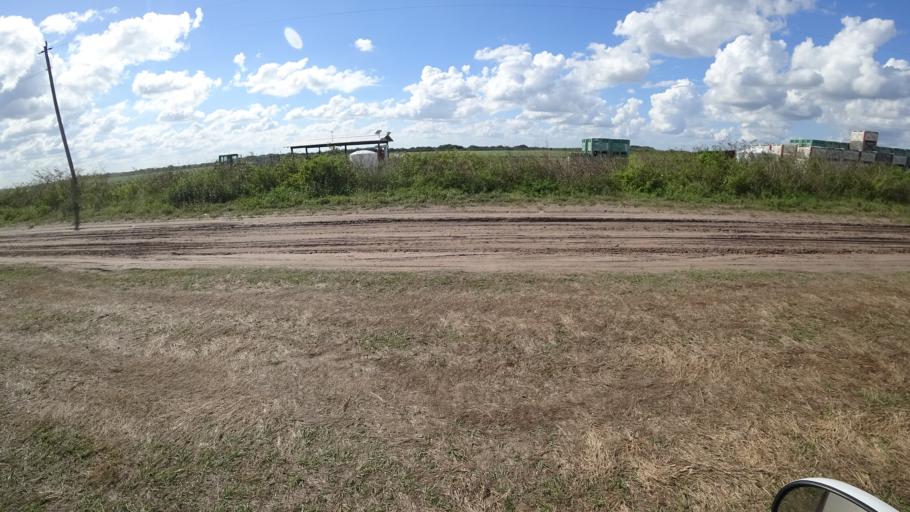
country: US
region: Florida
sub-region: DeSoto County
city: Arcadia
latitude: 27.3382
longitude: -82.0968
